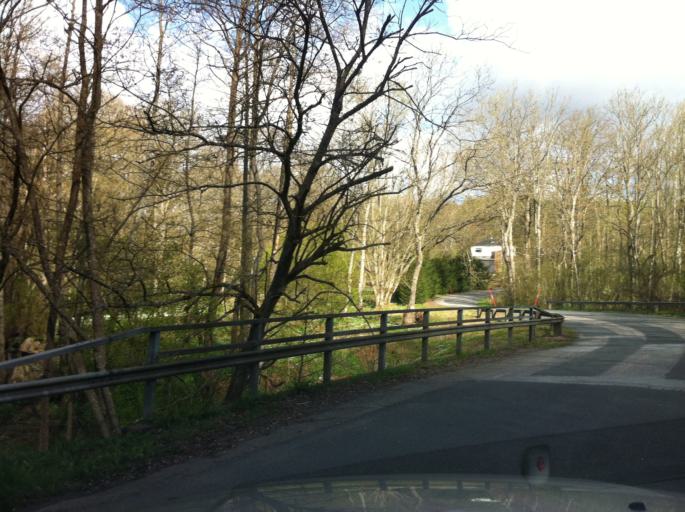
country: SE
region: Skane
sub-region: Hoors Kommun
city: Satofta
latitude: 55.9115
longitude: 13.6120
